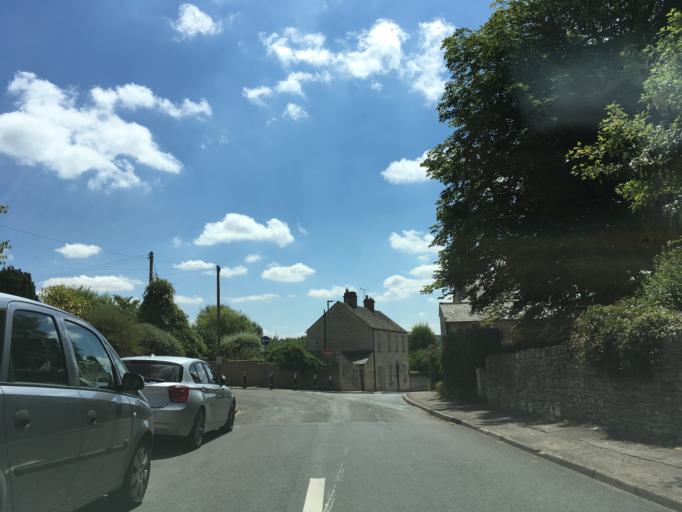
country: GB
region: England
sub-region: Gloucestershire
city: Painswick
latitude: 51.7901
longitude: -2.1949
